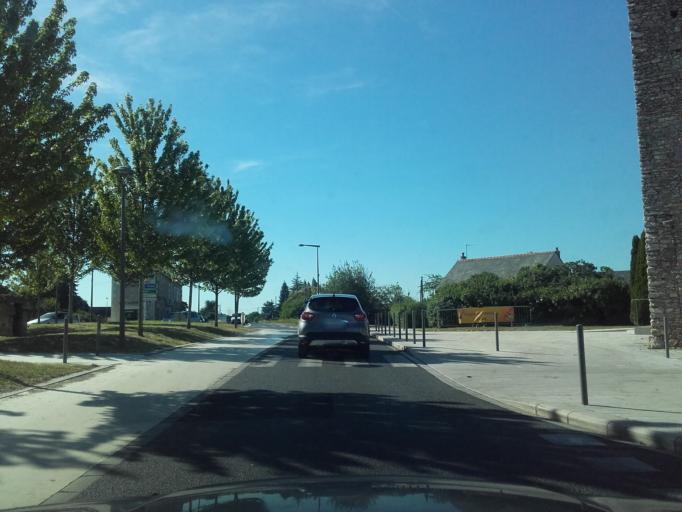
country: FR
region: Centre
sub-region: Departement d'Indre-et-Loire
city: Cormery
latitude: 47.2752
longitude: 0.8309
